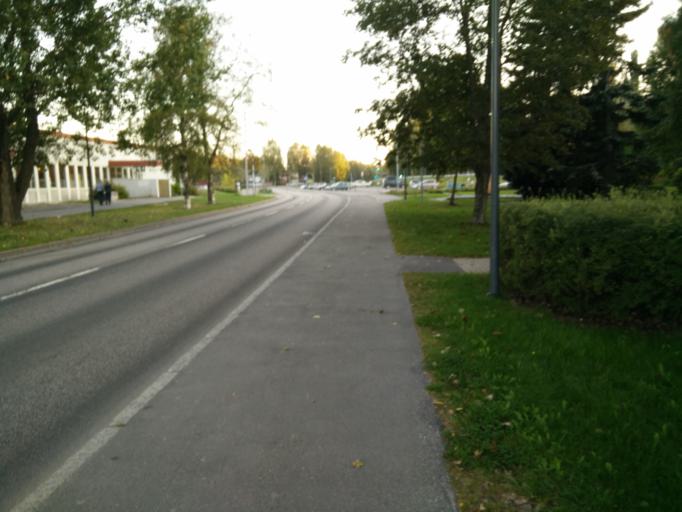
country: SE
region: Vaesternorrland
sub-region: Sundsvalls Kommun
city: Kvissleby
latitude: 62.2966
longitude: 17.3787
